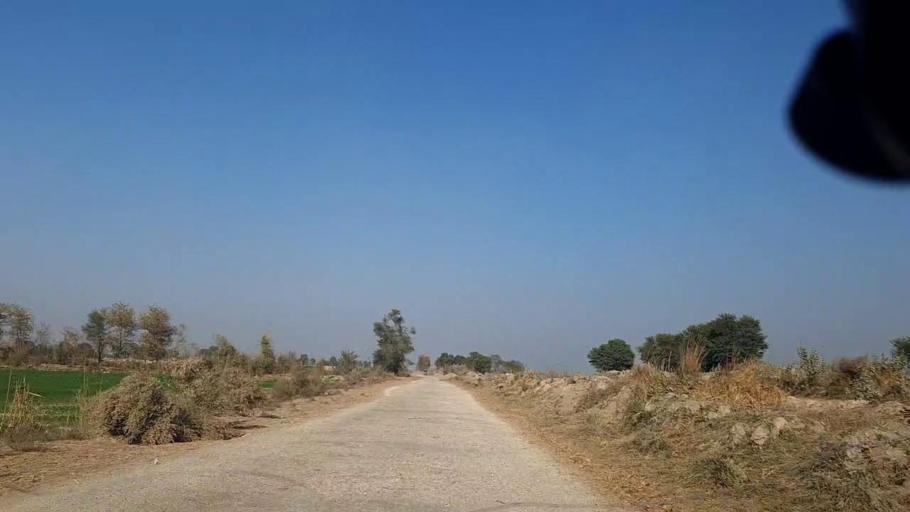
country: PK
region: Sindh
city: Khanpur
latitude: 27.6871
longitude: 69.4957
